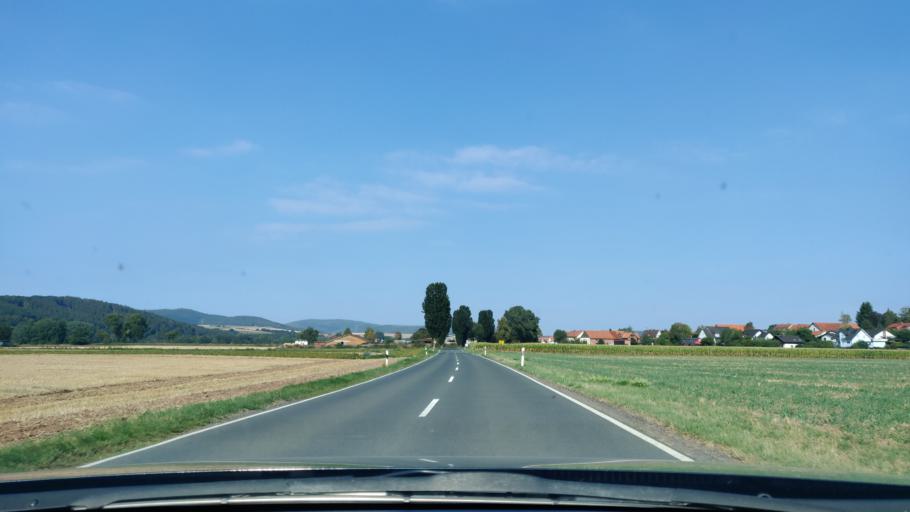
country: DE
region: Hesse
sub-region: Regierungsbezirk Kassel
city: Bad Wildungen
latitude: 51.1415
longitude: 9.1845
